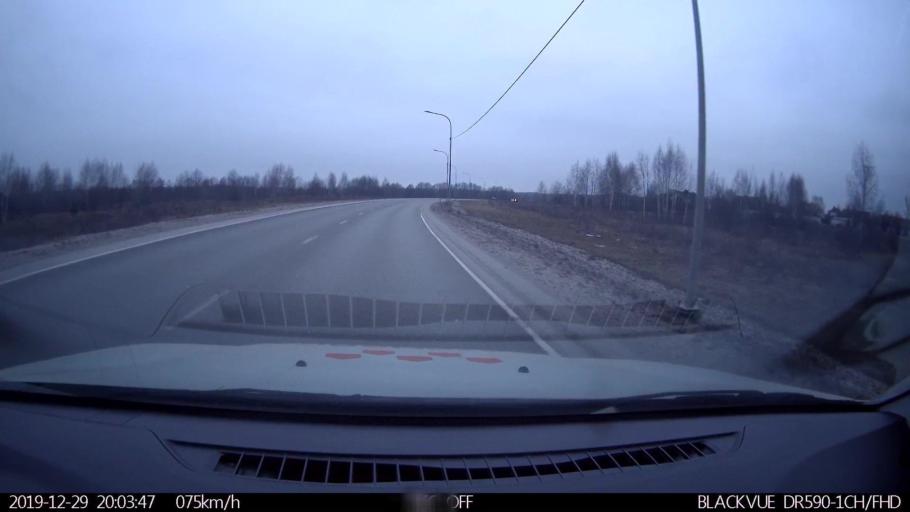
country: RU
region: Nizjnij Novgorod
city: Nizhniy Novgorod
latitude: 56.3767
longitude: 44.0133
